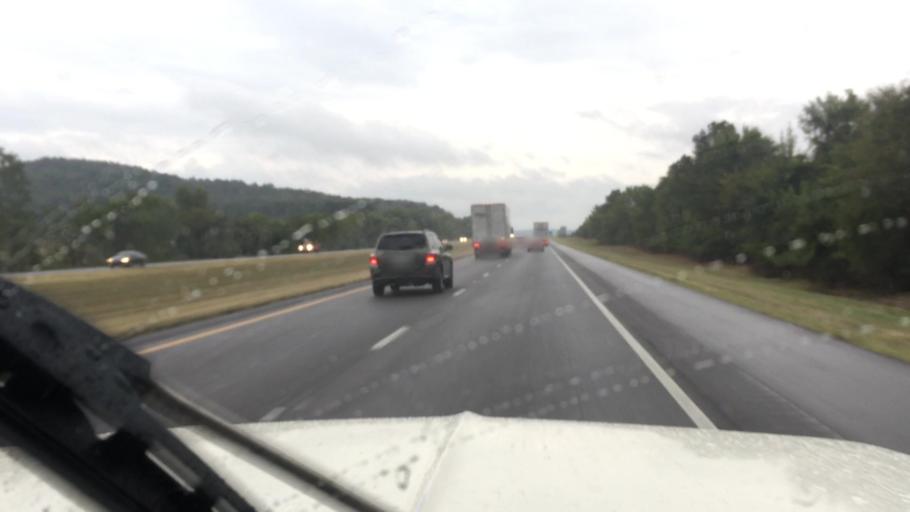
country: US
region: Alabama
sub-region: Morgan County
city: Falkville
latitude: 34.3934
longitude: -86.8961
